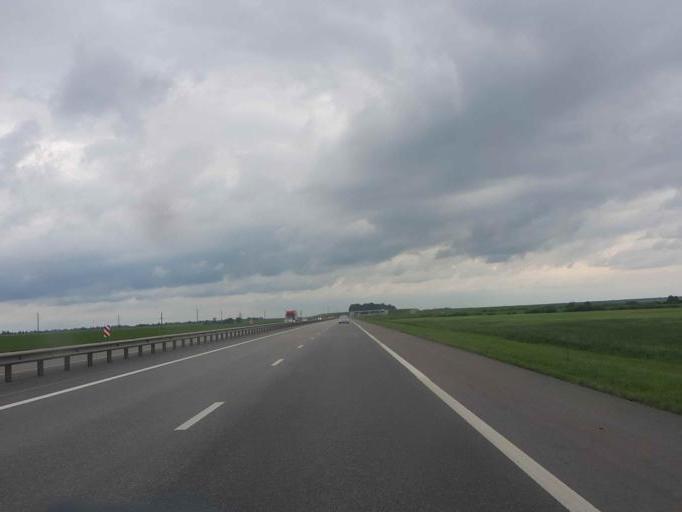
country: RU
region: Tambov
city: Selezni
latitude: 52.8283
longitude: 40.8981
